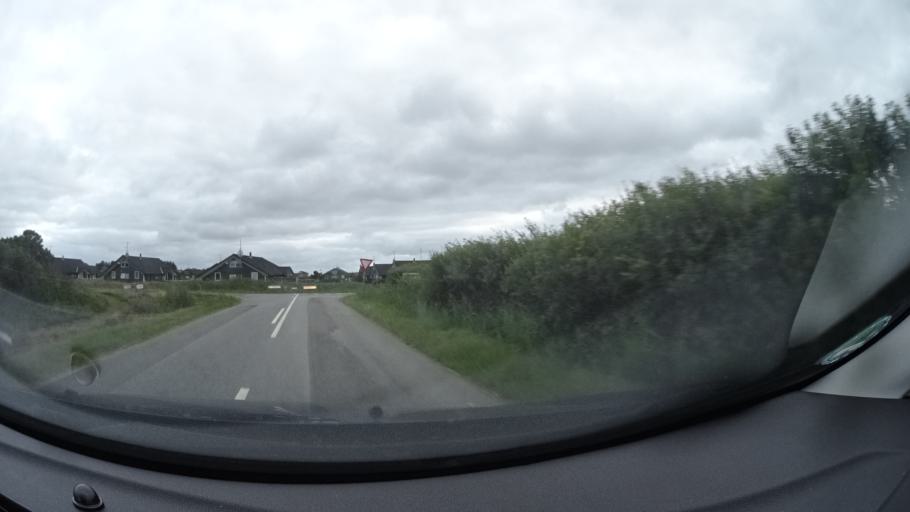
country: DK
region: Central Jutland
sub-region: Ringkobing-Skjern Kommune
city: Ringkobing
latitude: 56.1459
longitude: 8.1333
